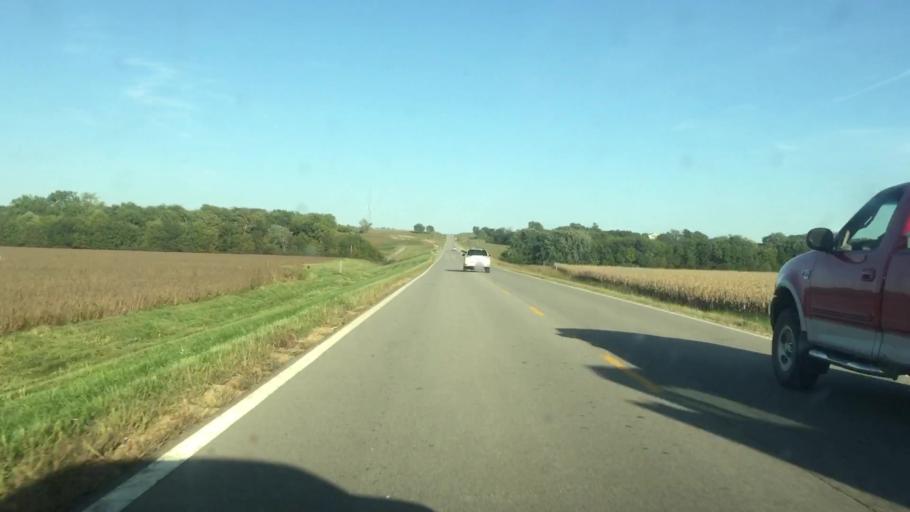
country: US
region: Kansas
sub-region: Brown County
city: Horton
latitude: 39.5875
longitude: -95.5599
